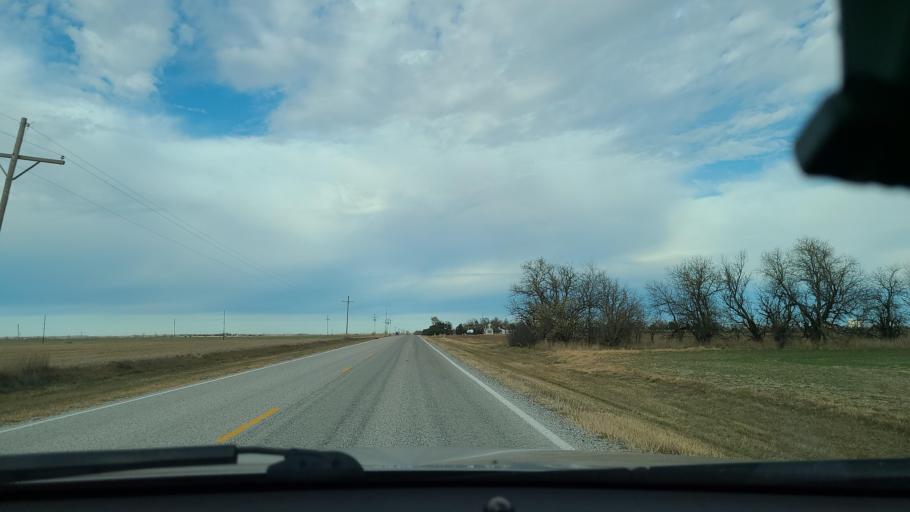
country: US
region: Kansas
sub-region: McPherson County
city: Inman
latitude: 38.3653
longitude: -97.9244
